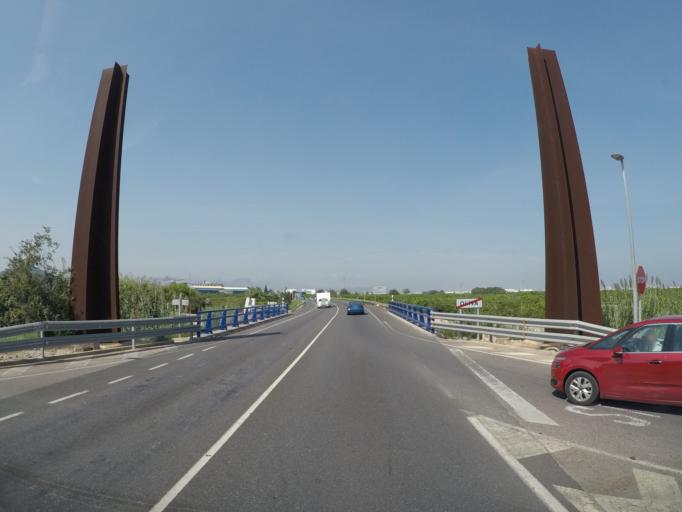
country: ES
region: Valencia
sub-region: Provincia de Valencia
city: Oliva
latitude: 38.9247
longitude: -0.1263
